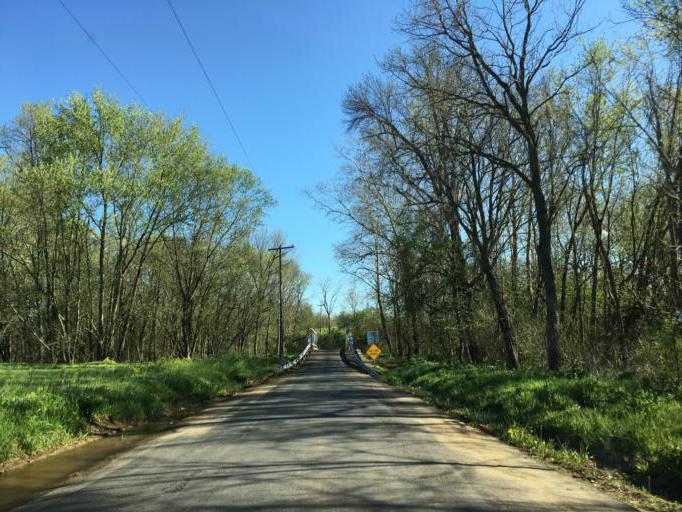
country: US
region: Maryland
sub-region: Frederick County
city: Emmitsburg
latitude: 39.6917
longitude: -77.3172
